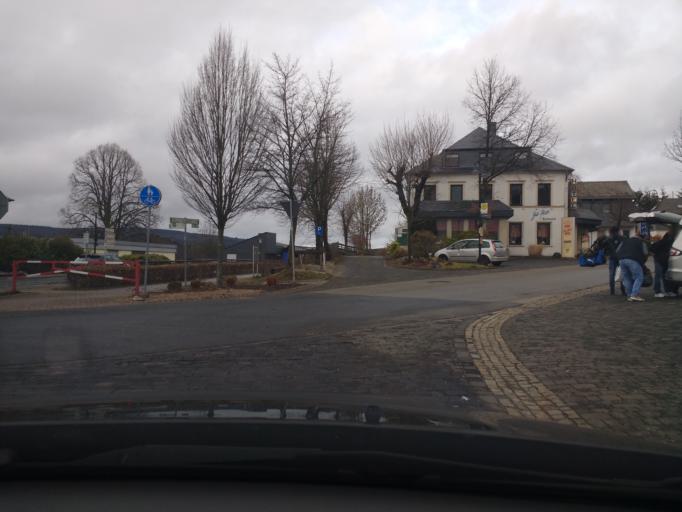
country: DE
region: Rheinland-Pfalz
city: Kell
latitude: 49.6348
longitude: 6.8268
